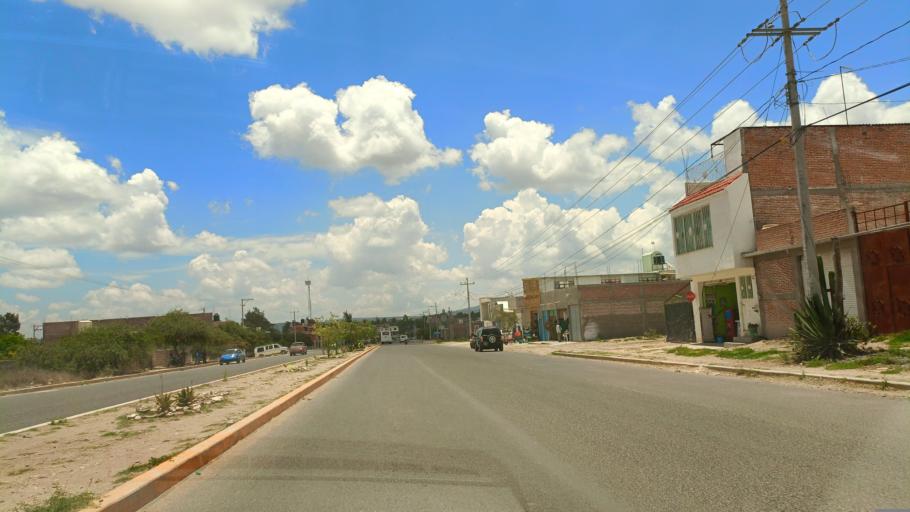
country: MX
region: Guanajuato
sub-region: San Luis de la Paz
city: San Luis de la Paz
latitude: 21.2898
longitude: -100.4959
